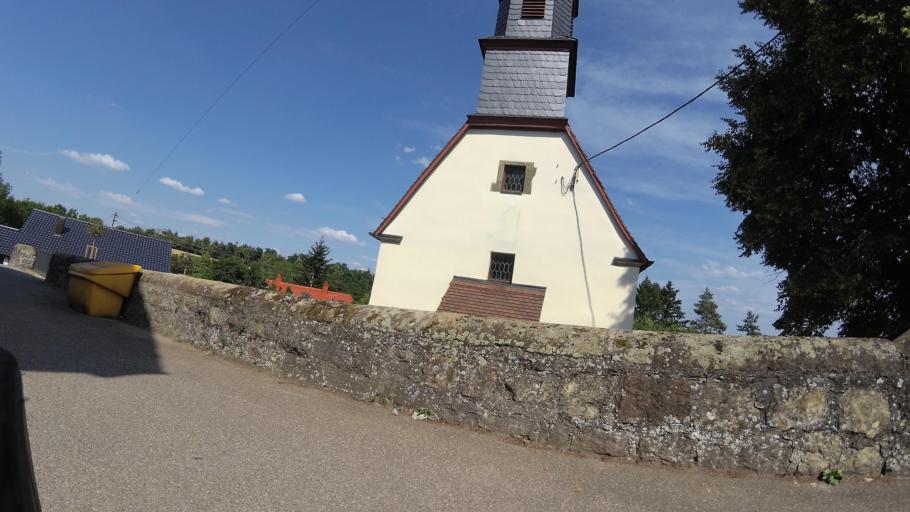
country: DE
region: Baden-Wuerttemberg
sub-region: Regierungsbezirk Stuttgart
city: Offenau
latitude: 49.2440
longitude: 9.1400
